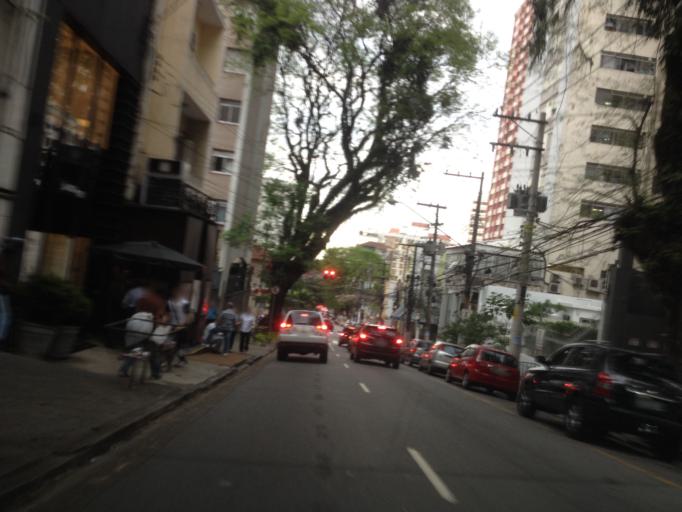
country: BR
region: Sao Paulo
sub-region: Sao Paulo
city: Sao Paulo
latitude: -23.5587
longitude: -46.6662
